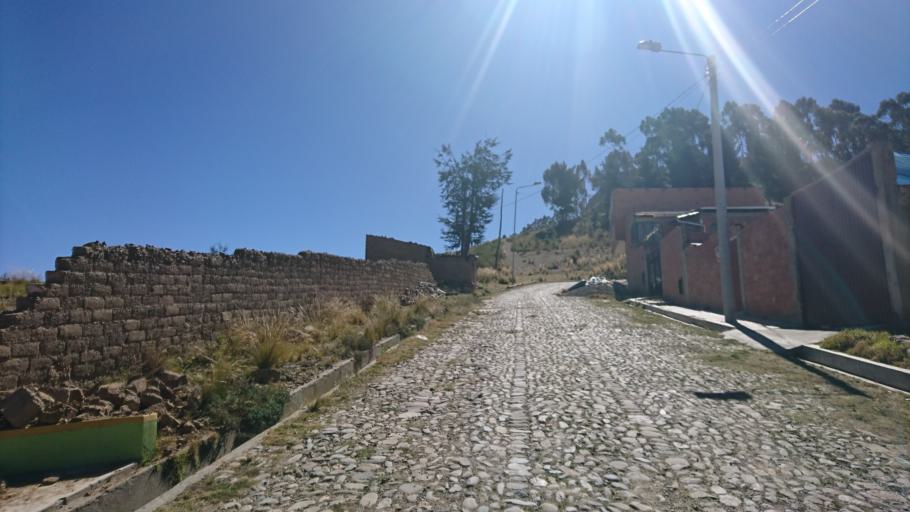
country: BO
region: La Paz
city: La Paz
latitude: -16.4872
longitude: -68.1050
